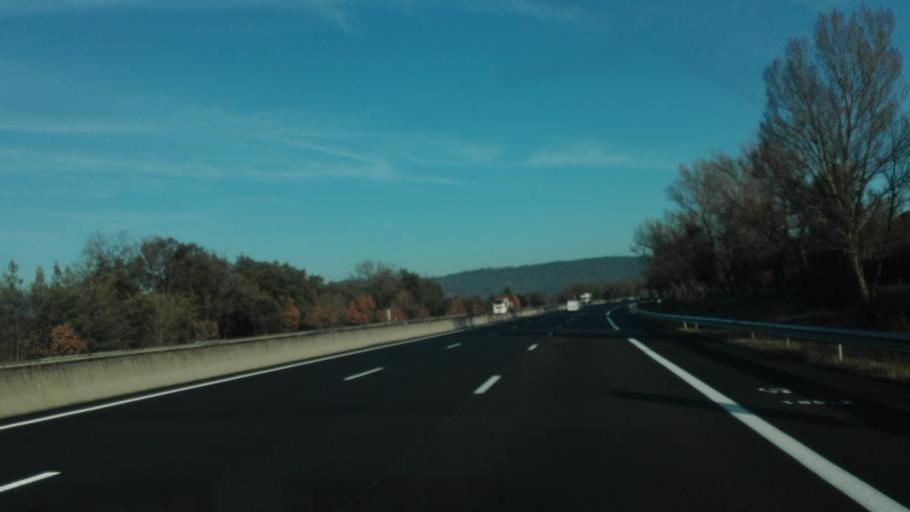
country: FR
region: Provence-Alpes-Cote d'Azur
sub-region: Departement du Var
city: Les Arcs
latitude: 43.4293
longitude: 6.4671
